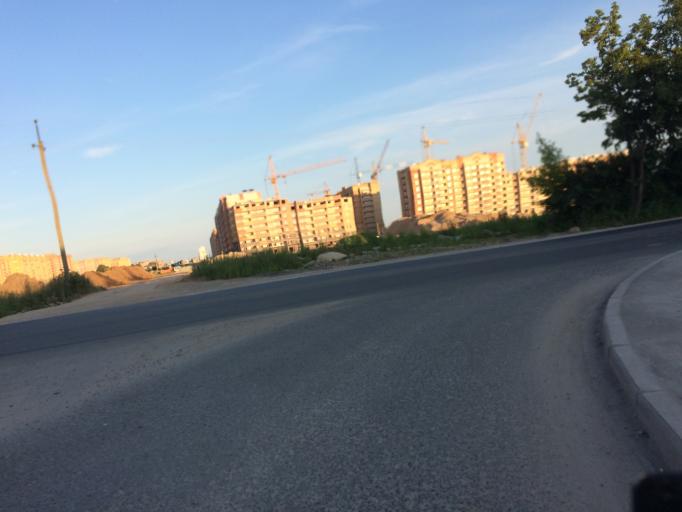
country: RU
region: Mariy-El
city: Medvedevo
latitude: 56.6411
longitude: 47.8319
